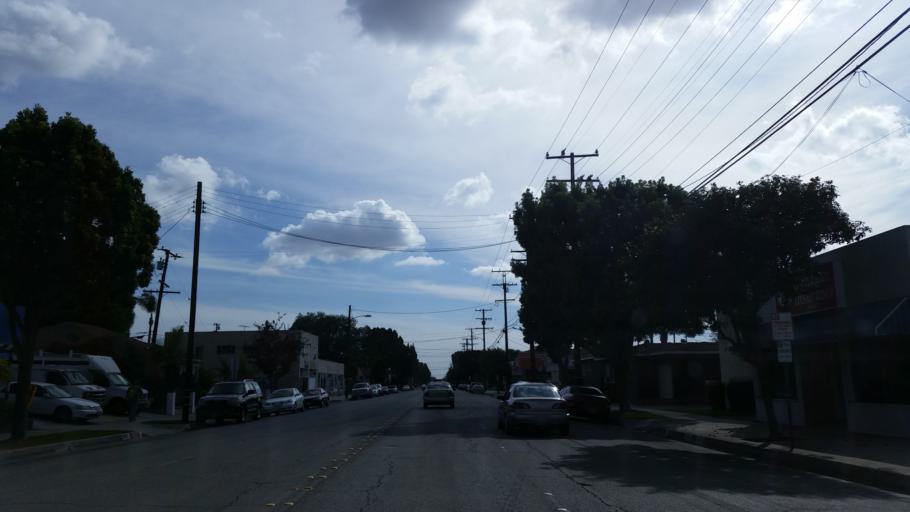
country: US
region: California
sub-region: Los Angeles County
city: Bellflower
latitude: 33.8879
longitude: -118.1340
